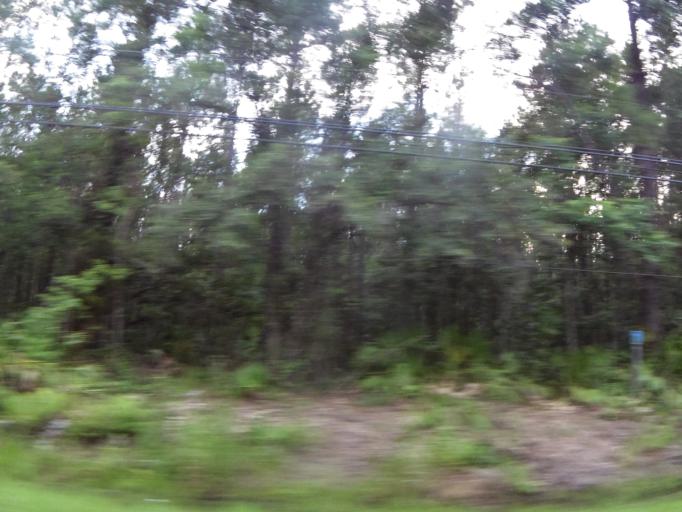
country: US
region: Florida
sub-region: Duval County
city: Jacksonville
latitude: 30.3627
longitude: -81.7732
